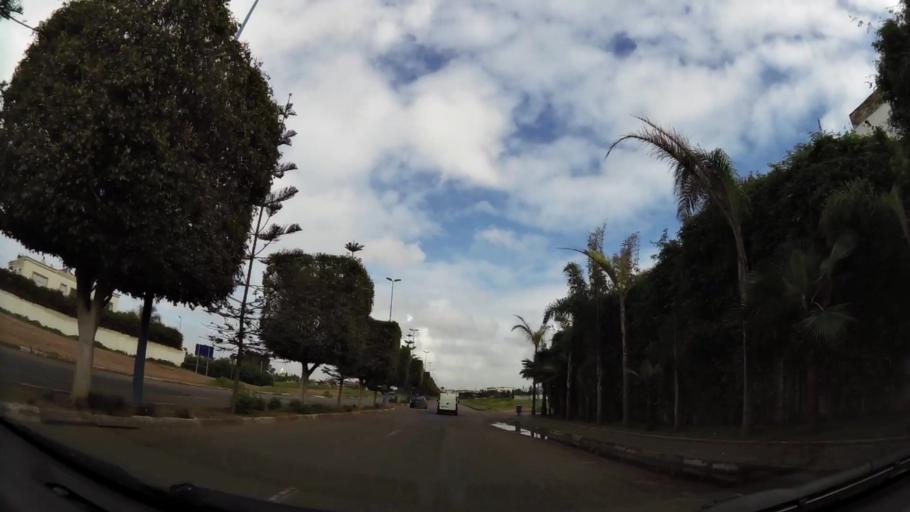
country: MA
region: Grand Casablanca
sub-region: Casablanca
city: Casablanca
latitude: 33.5406
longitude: -7.6344
